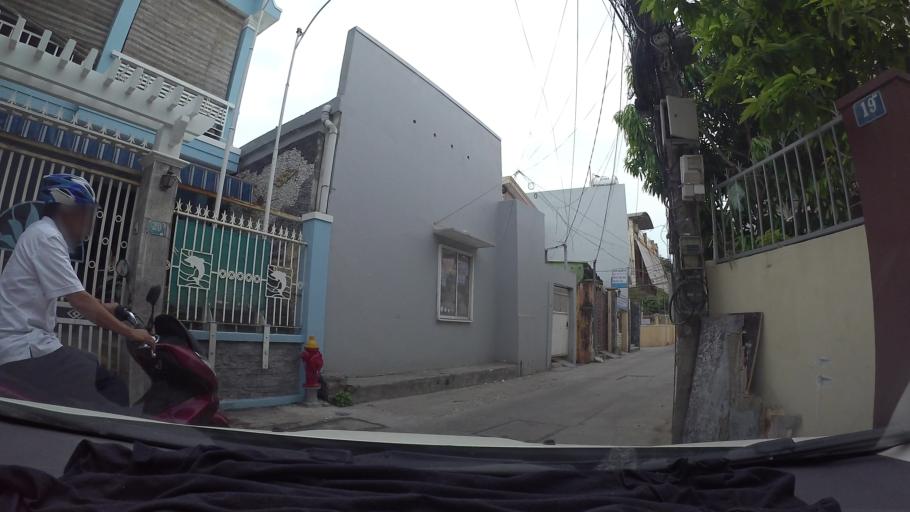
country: VN
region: Da Nang
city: Da Nang
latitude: 16.0838
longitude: 108.2195
